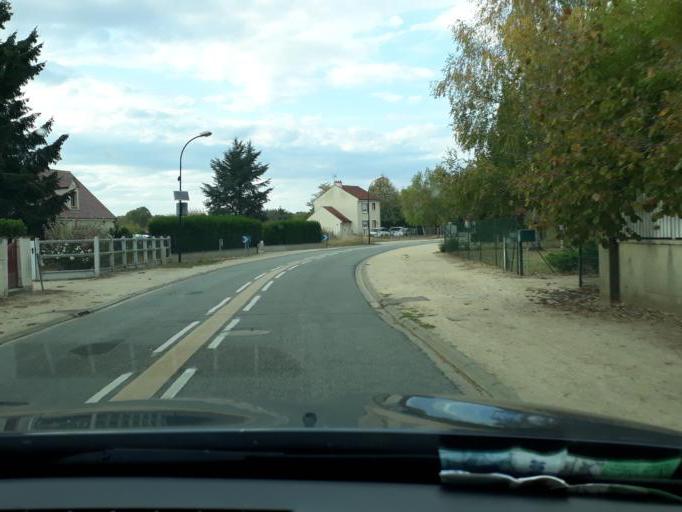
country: FR
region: Centre
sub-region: Departement du Loiret
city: Saint-Benoit-sur-Loire
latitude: 47.8140
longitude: 2.3015
